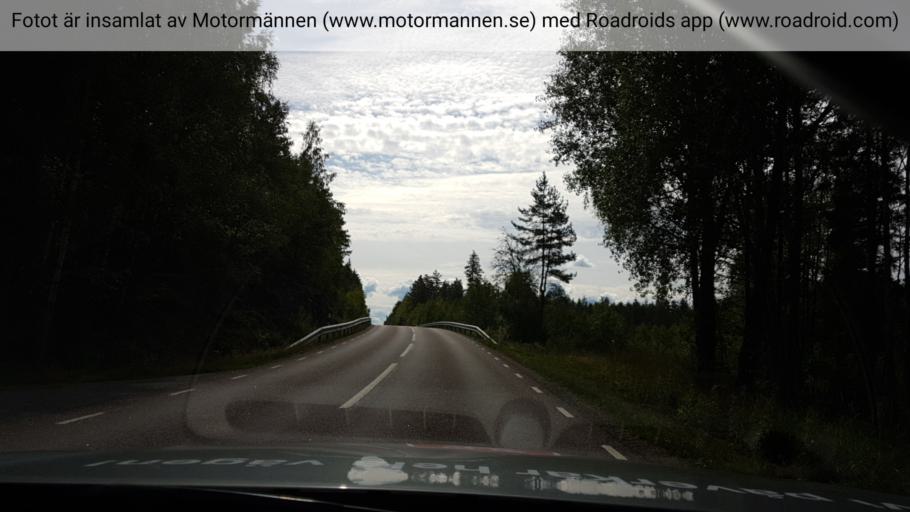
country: SE
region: Uppsala
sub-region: Heby Kommun
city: OEstervala
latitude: 60.0083
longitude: 17.2948
